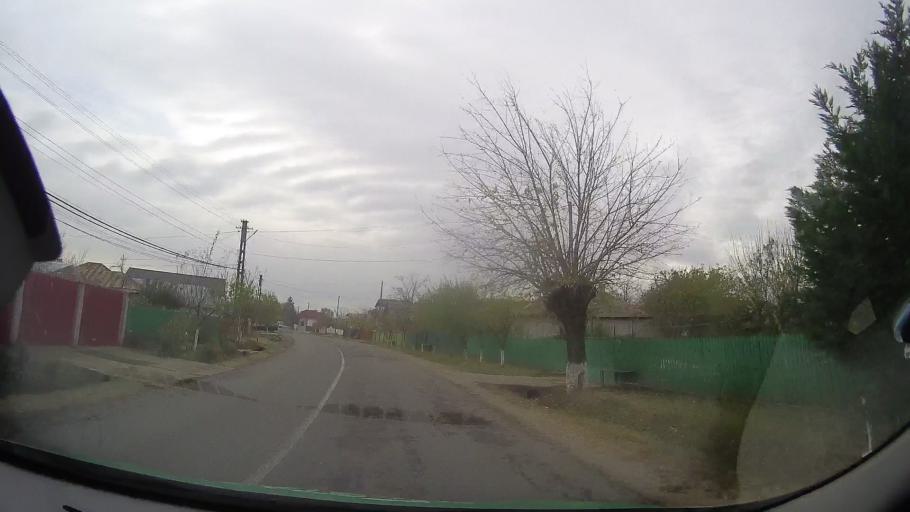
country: RO
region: Prahova
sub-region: Comuna Valea Calugareasca
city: Pantazi
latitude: 44.9221
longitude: 26.1554
